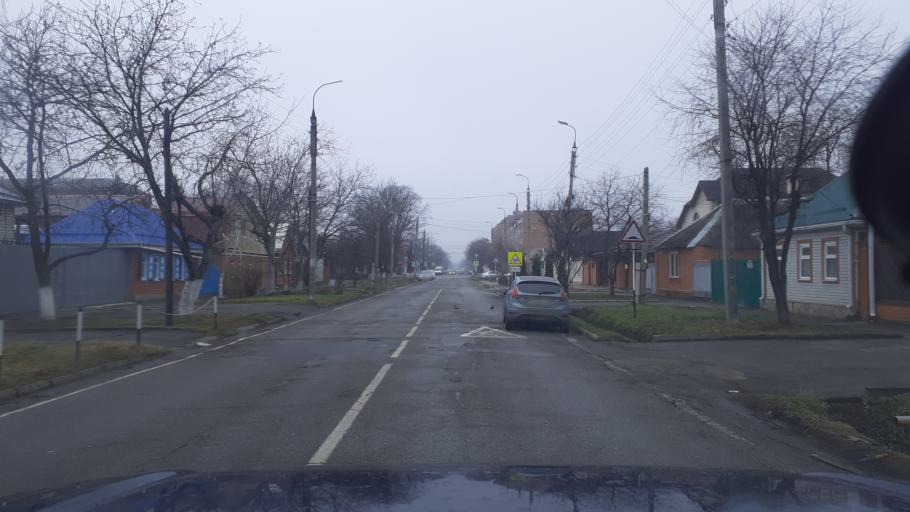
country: RU
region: Adygeya
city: Maykop
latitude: 44.6168
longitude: 40.1114
